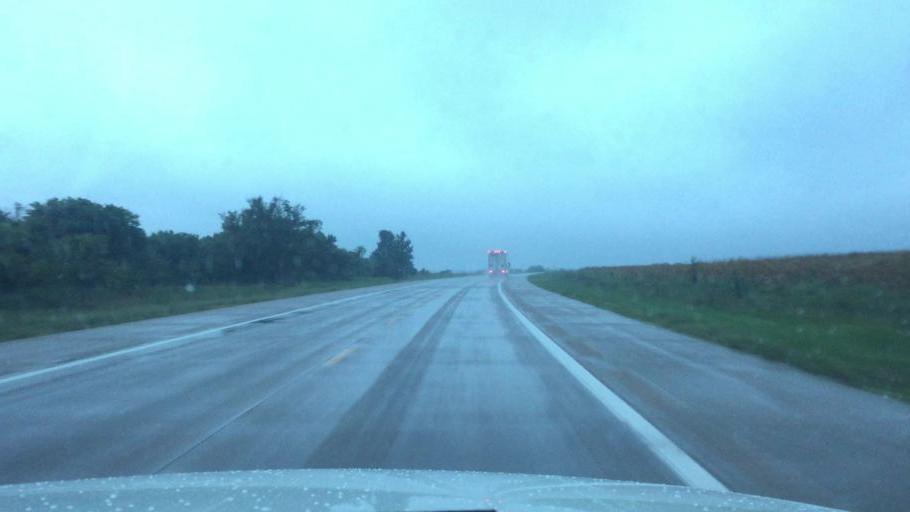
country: US
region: Kansas
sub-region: Neosho County
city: Chanute
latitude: 37.5371
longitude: -95.4708
